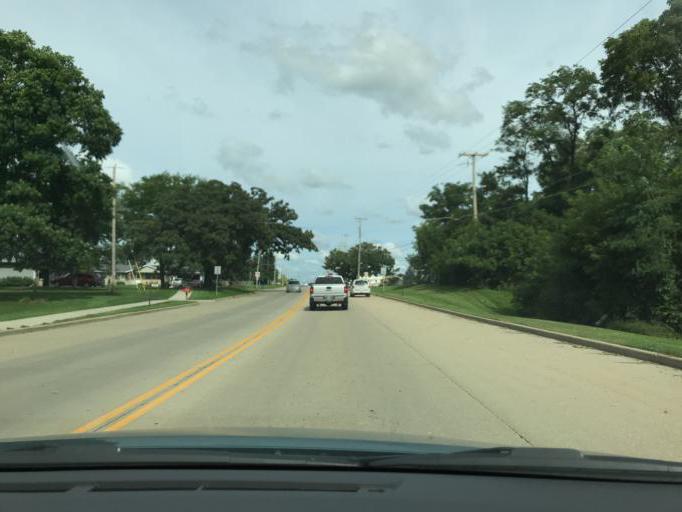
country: US
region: Wisconsin
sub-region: Racine County
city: Burlington
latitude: 42.6630
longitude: -88.2627
